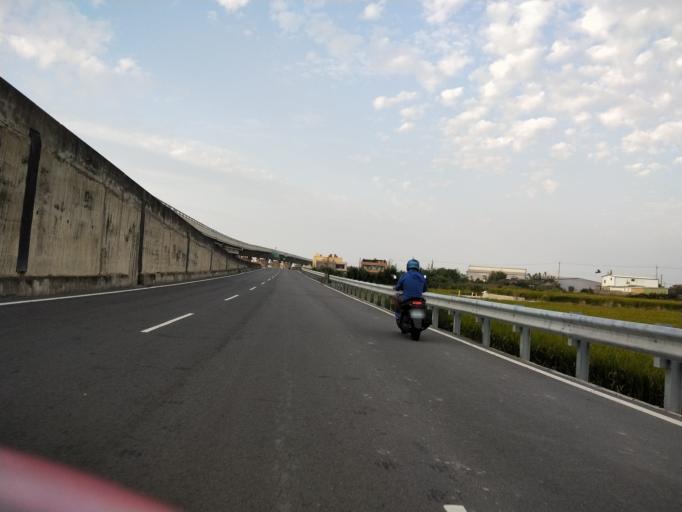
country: TW
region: Taiwan
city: Fengyuan
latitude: 24.4084
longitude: 120.6151
